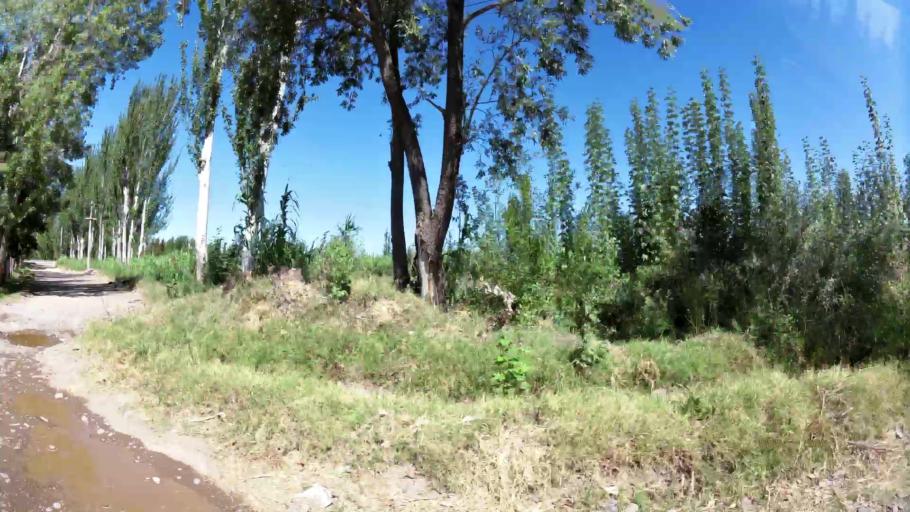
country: AR
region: Mendoza
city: Lujan de Cuyo
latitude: -32.9908
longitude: -68.8537
